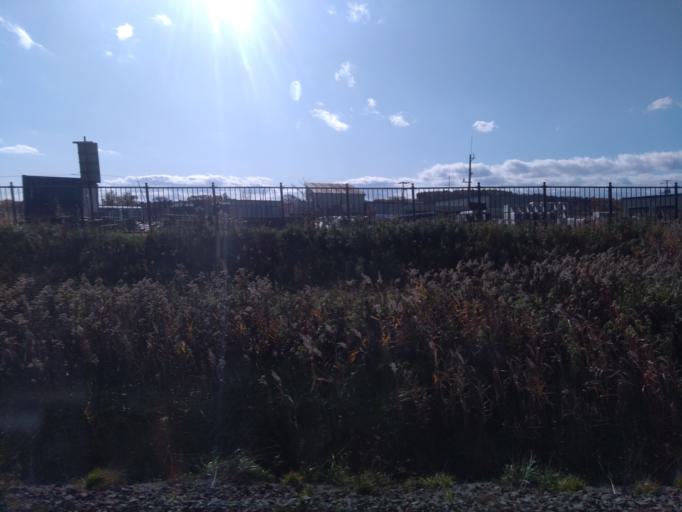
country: JP
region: Hokkaido
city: Kitahiroshima
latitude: 42.9929
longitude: 141.5531
